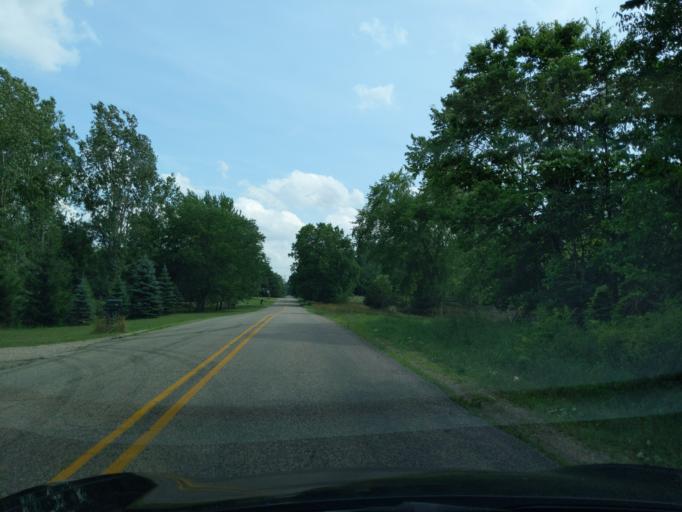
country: US
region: Michigan
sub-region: Eaton County
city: Dimondale
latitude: 42.5768
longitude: -84.6022
